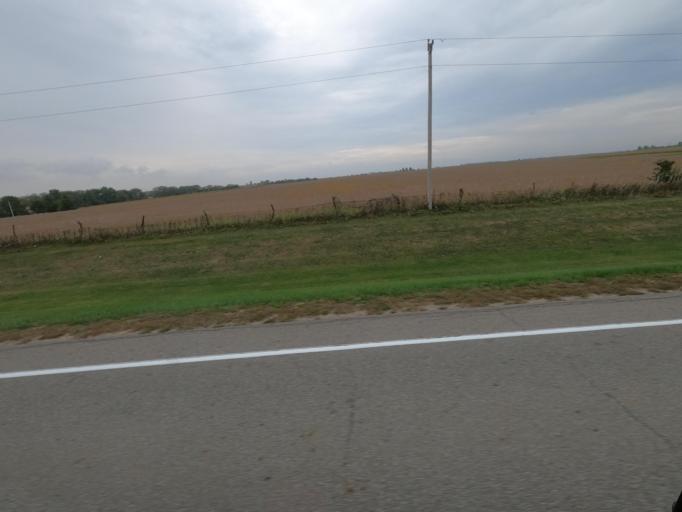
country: US
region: Iowa
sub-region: Van Buren County
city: Keosauqua
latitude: 40.8133
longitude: -91.7890
